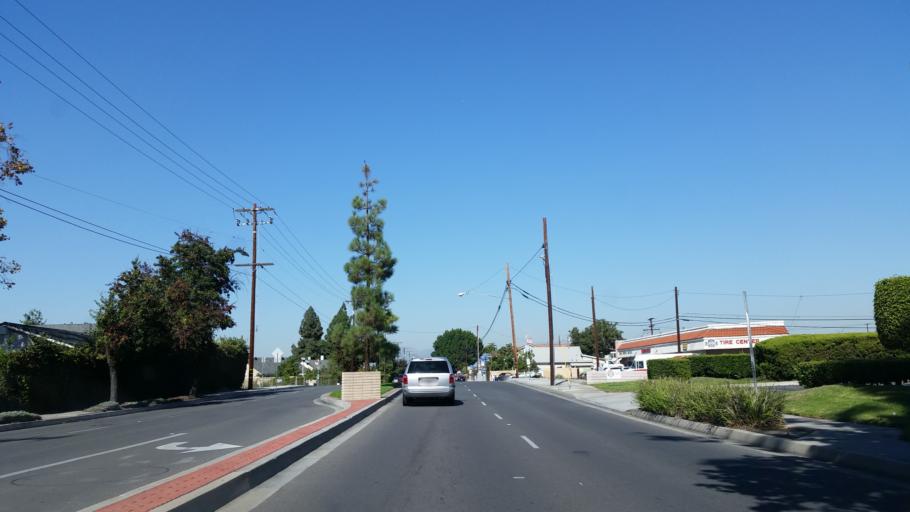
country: US
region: California
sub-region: Los Angeles County
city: Cerritos
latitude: 33.8536
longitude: -118.0722
